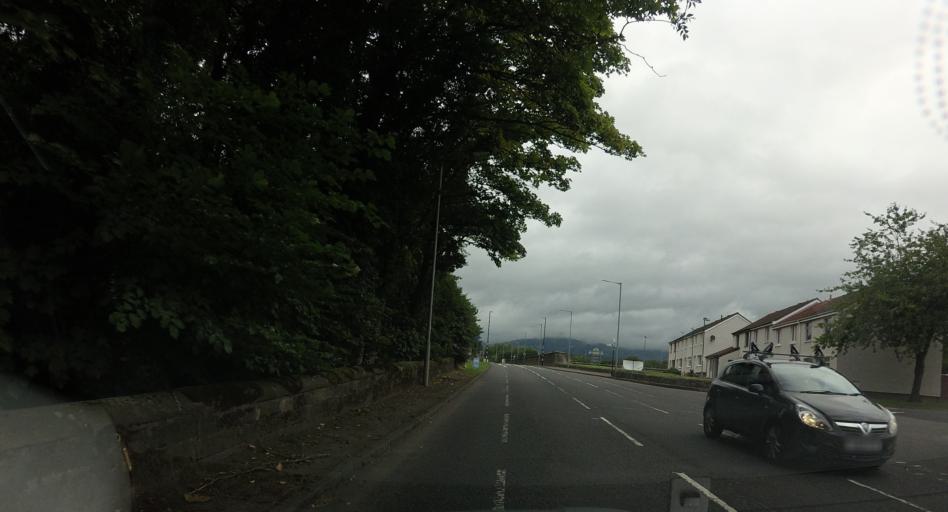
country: GB
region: Scotland
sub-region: Clackmannanshire
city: Clackmannan
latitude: 56.1119
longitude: -3.7570
